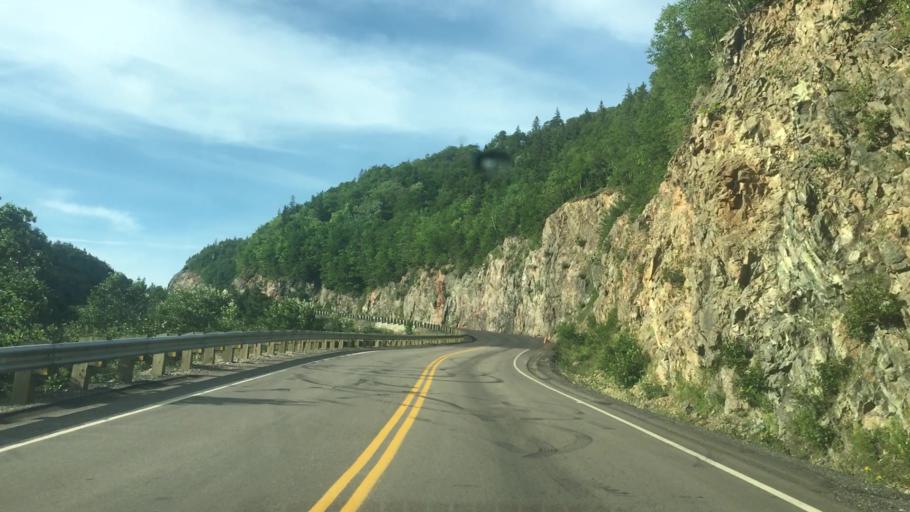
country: CA
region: Nova Scotia
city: Sydney Mines
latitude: 46.8163
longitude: -60.6512
